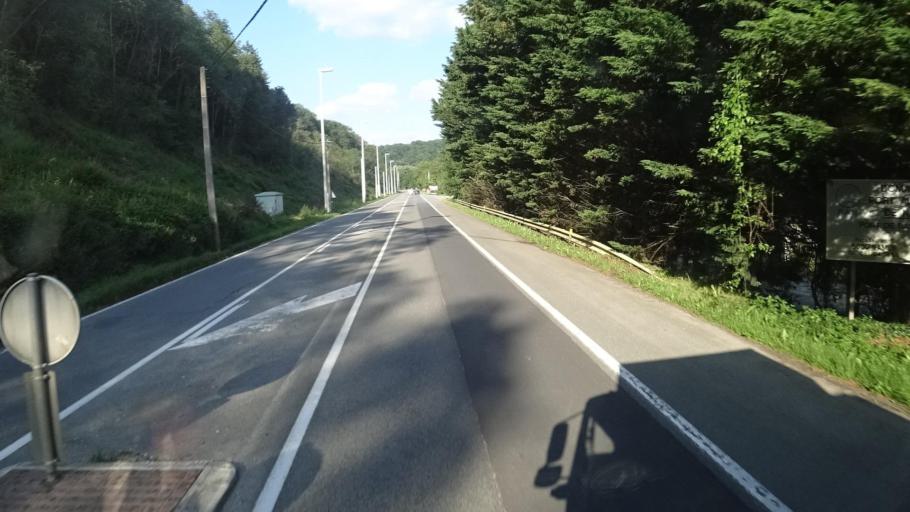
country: BE
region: Wallonia
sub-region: Province de Namur
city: Profondeville
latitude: 50.3526
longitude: 4.8688
